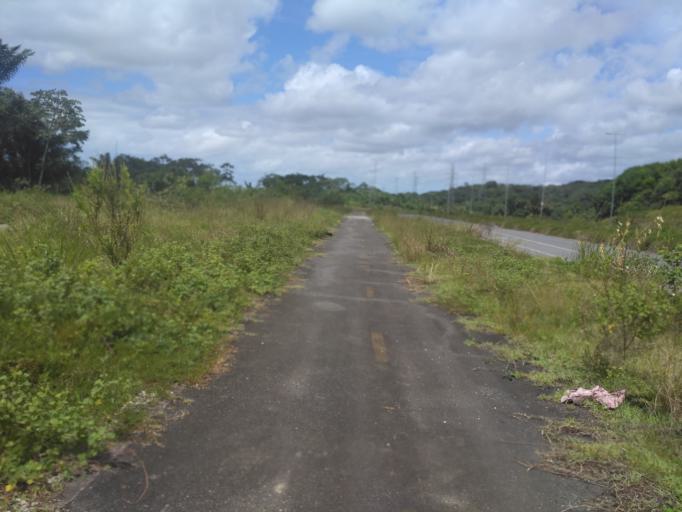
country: BR
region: Pernambuco
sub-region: Sao Lourenco Da Mata
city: Sao Lourenco da Mata
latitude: -8.0402
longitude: -34.9983
